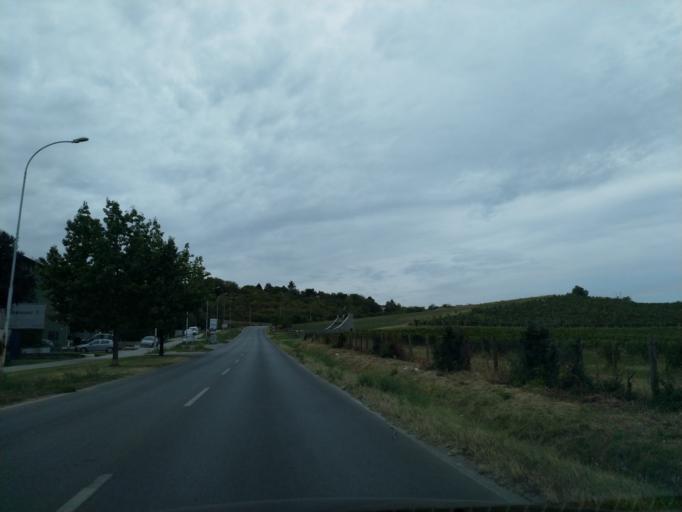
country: RS
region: Central Serbia
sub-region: Pomoravski Okrug
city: Jagodina
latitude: 43.9871
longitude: 21.2400
